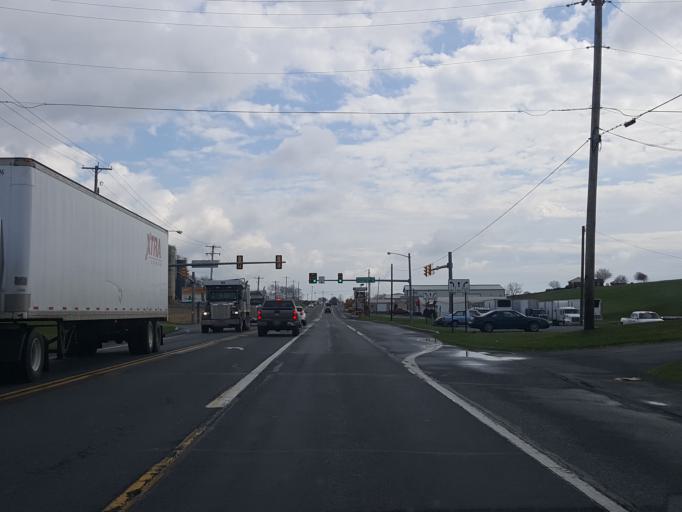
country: US
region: Pennsylvania
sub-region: Lebanon County
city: Myerstown
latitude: 40.3827
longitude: -76.2895
